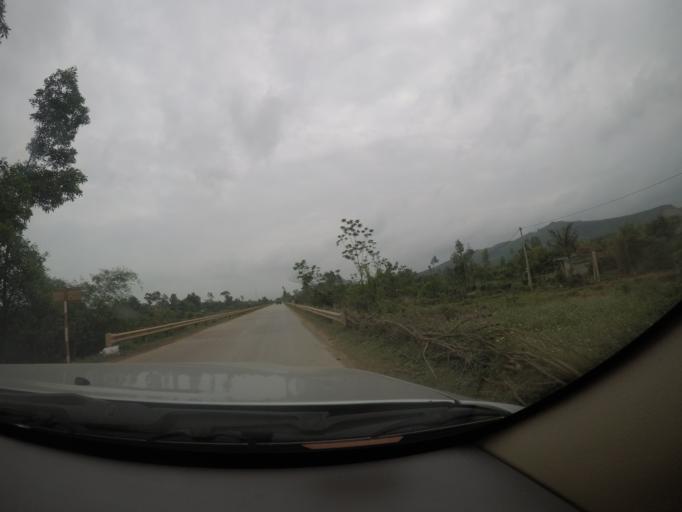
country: VN
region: Quang Binh
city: Quan Hau
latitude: 17.2866
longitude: 106.6471
